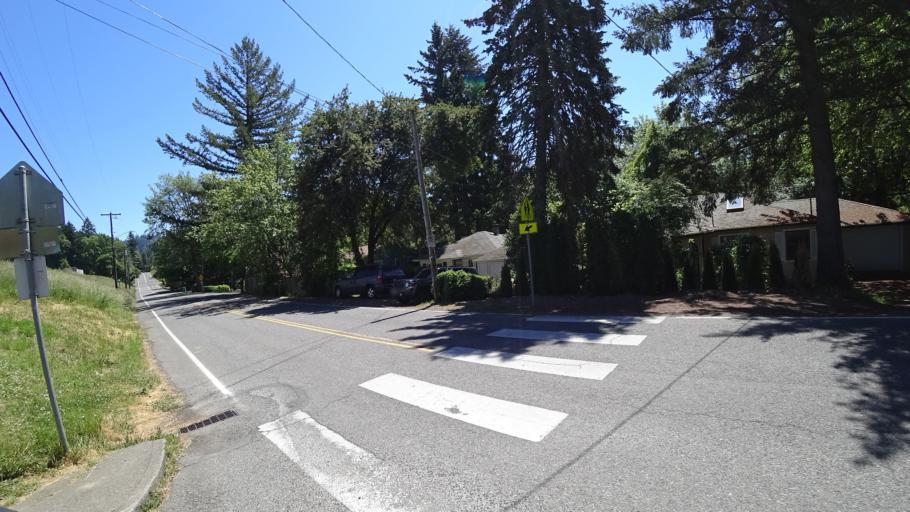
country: US
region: Oregon
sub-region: Washington County
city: Raleigh Hills
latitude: 45.4907
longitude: -122.7256
